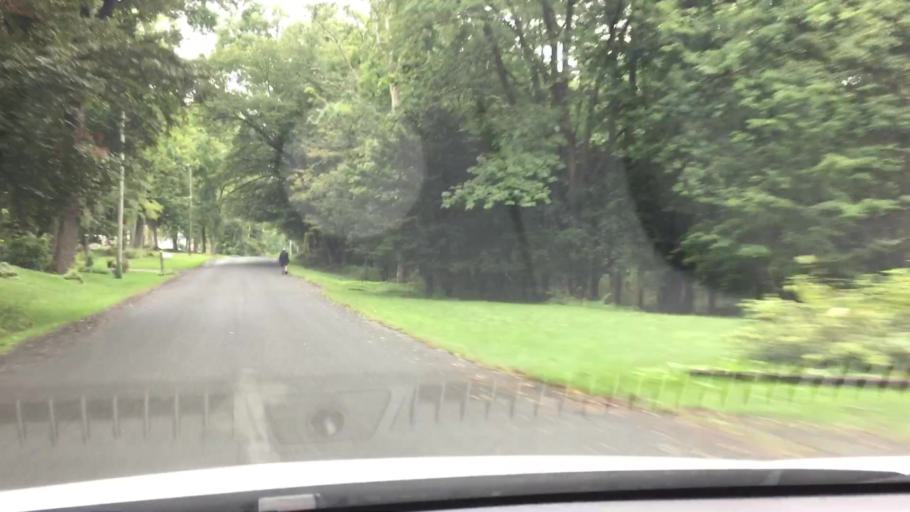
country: US
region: Massachusetts
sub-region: Berkshire County
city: Richmond
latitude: 42.3614
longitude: -73.3679
